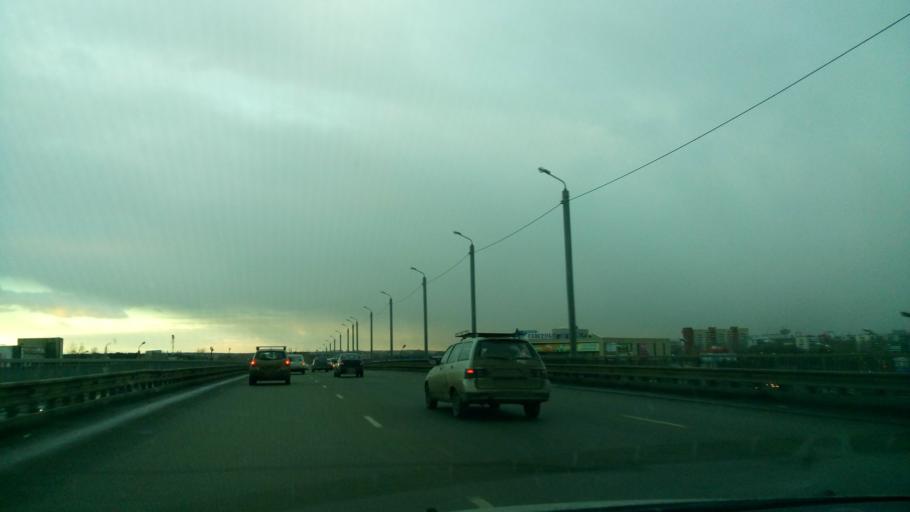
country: RU
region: Chelyabinsk
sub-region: Gorod Chelyabinsk
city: Chelyabinsk
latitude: 55.2278
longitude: 61.3742
